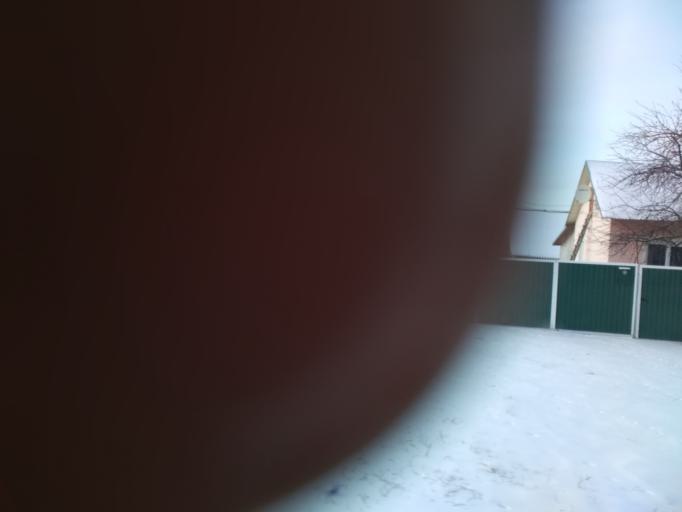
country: RU
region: Bashkortostan
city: Iglino
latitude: 54.7704
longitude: 56.5345
